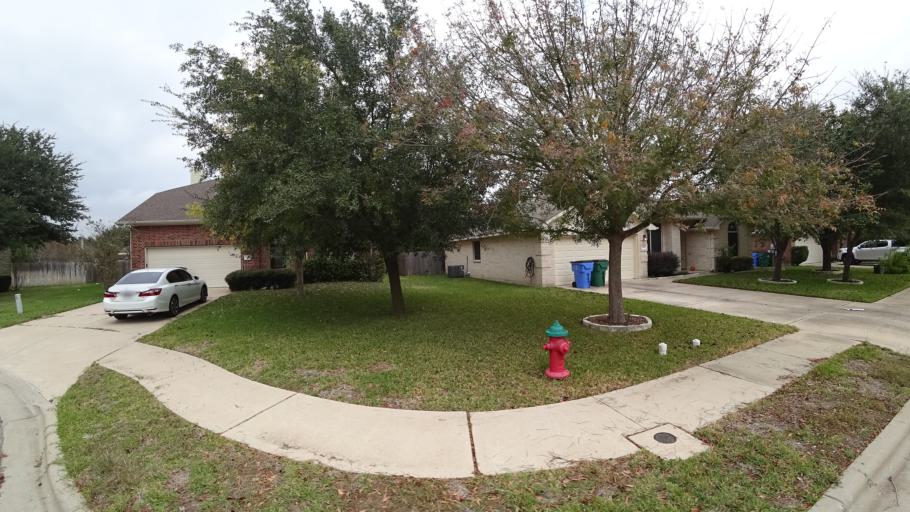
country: US
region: Texas
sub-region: Travis County
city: Pflugerville
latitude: 30.4379
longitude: -97.6047
